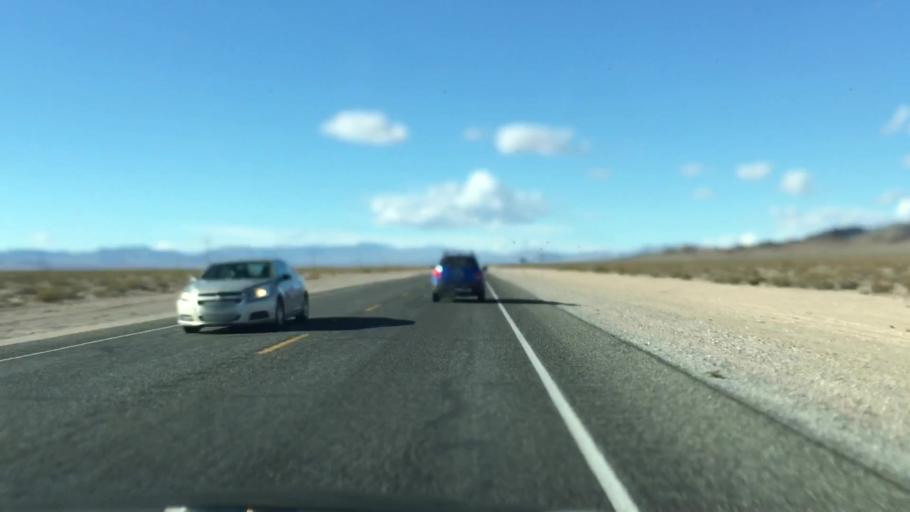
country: US
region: Nevada
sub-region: Nye County
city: Beatty
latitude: 36.7142
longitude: -116.6052
